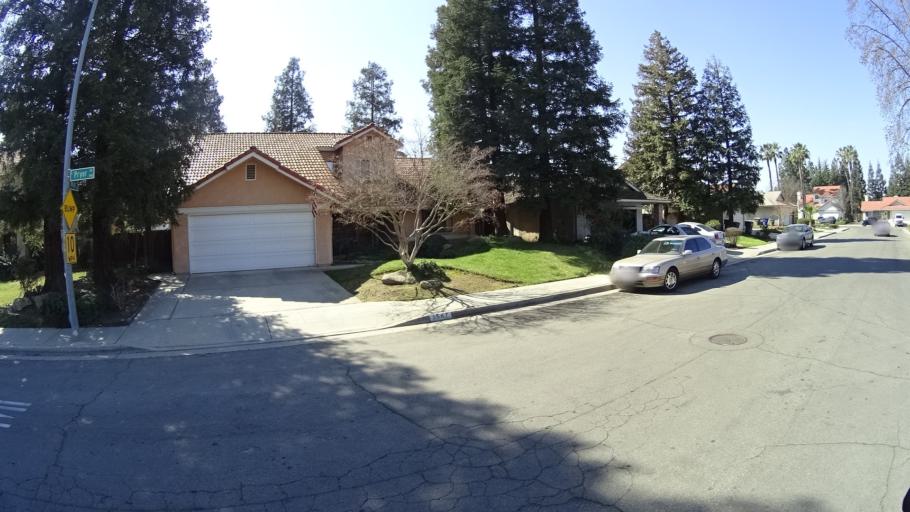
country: US
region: California
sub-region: Fresno County
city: Clovis
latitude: 36.8706
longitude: -119.7555
